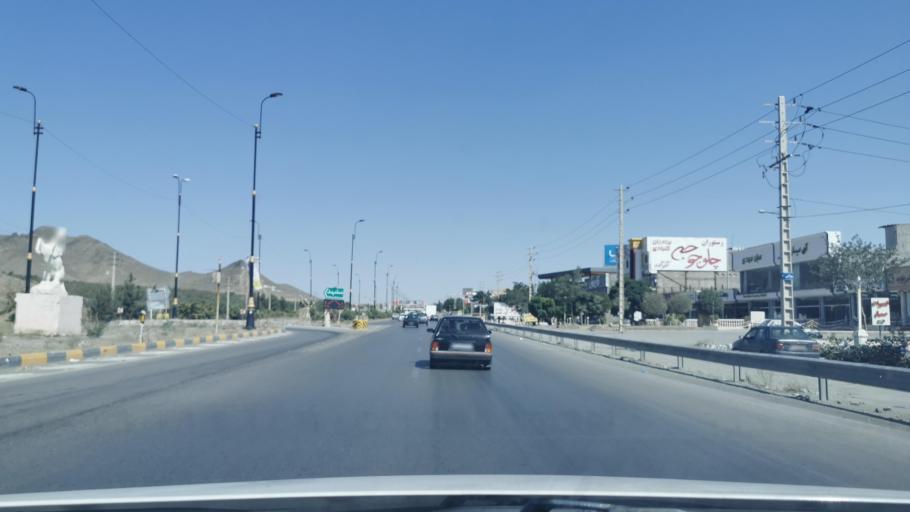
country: IR
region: Razavi Khorasan
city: Torqabeh
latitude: 36.3892
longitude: 59.4074
